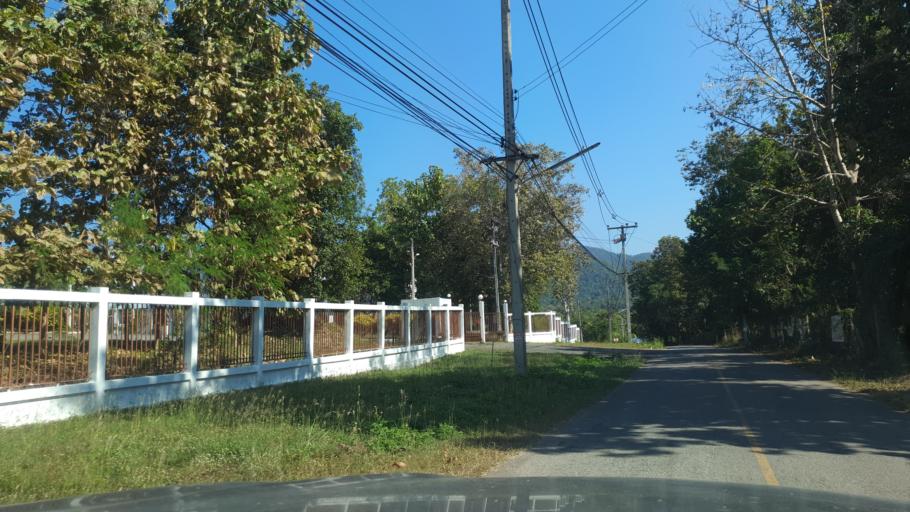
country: TH
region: Chiang Mai
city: San Sai
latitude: 18.8849
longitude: 99.1638
